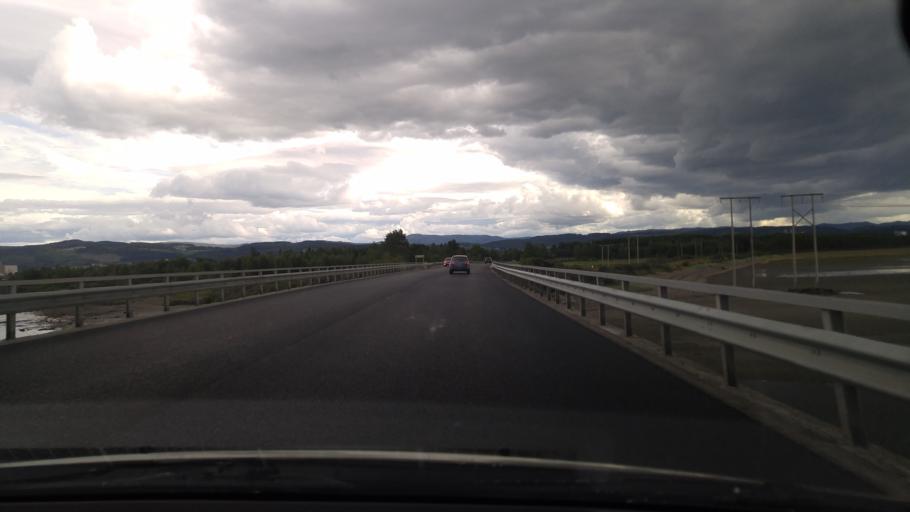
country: NO
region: Nord-Trondelag
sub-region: Verdal
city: Verdal
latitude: 63.8032
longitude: 11.4592
